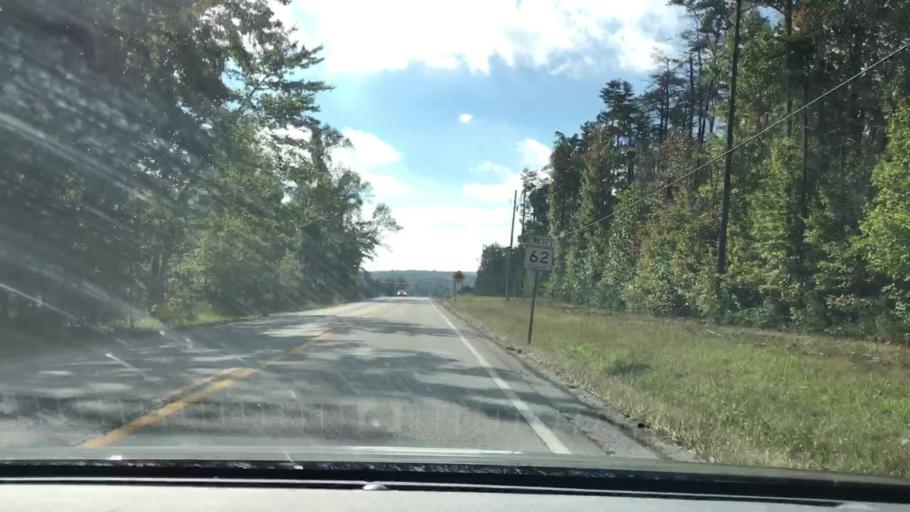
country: US
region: Tennessee
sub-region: Putnam County
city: Monterey
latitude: 36.1196
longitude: -85.1779
